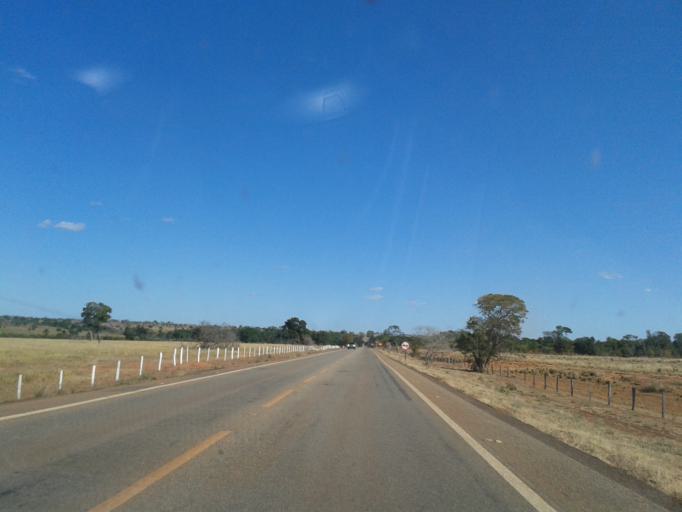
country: BR
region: Goias
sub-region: Crixas
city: Crixas
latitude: -14.2121
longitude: -50.3913
